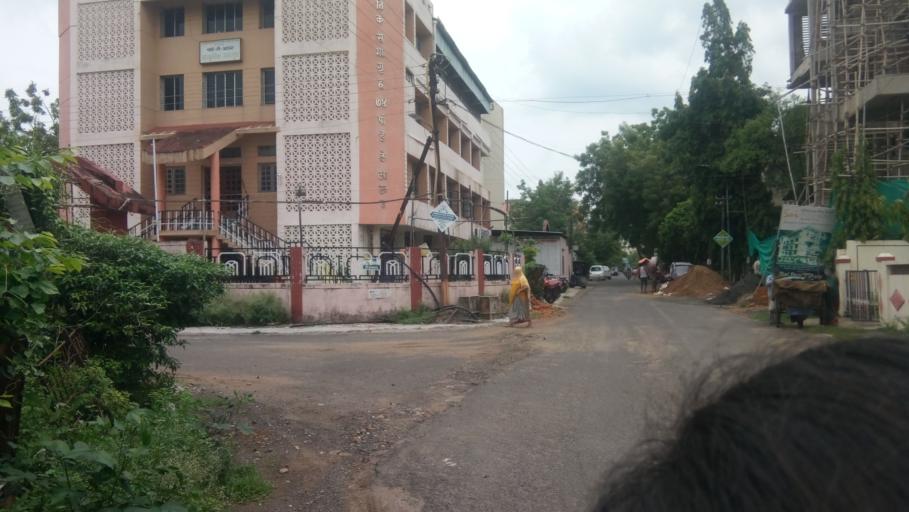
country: IN
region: Maharashtra
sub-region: Nagpur Division
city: Nagpur
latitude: 21.1086
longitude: 79.0636
